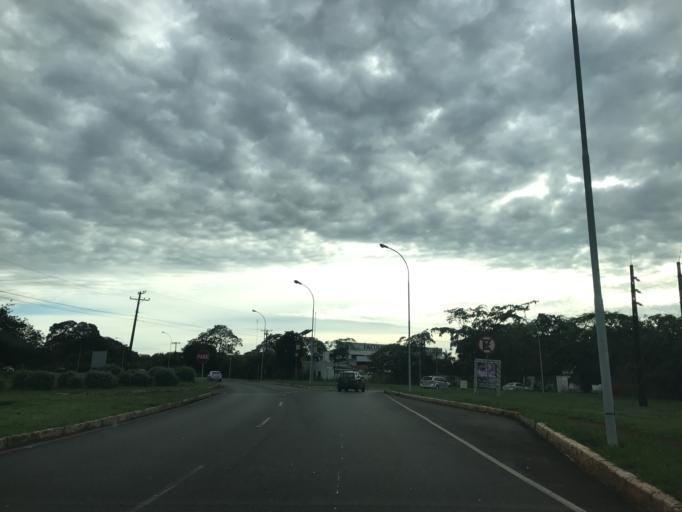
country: BR
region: Federal District
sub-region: Brasilia
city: Brasilia
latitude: -15.8117
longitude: -47.9169
